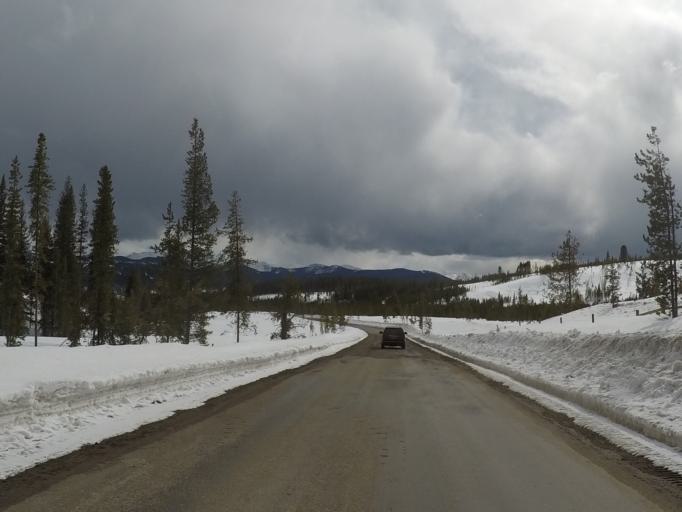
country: US
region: Montana
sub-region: Granite County
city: Philipsburg
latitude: 46.2175
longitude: -113.2570
